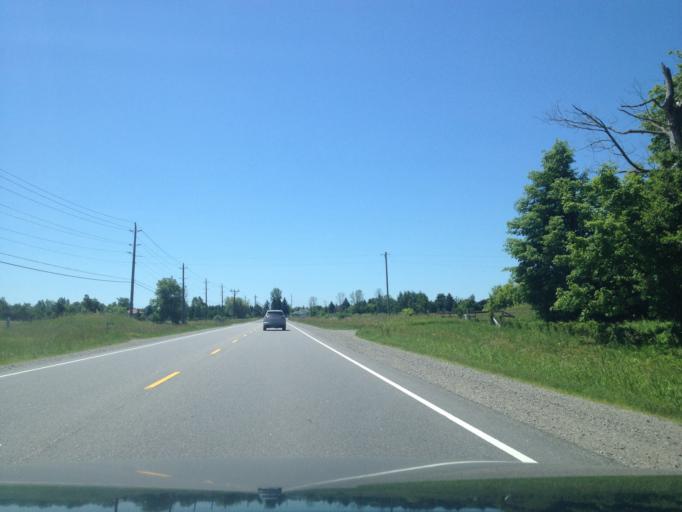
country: CA
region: Ontario
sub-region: Wellington County
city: Guelph
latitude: 43.6055
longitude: -80.1119
